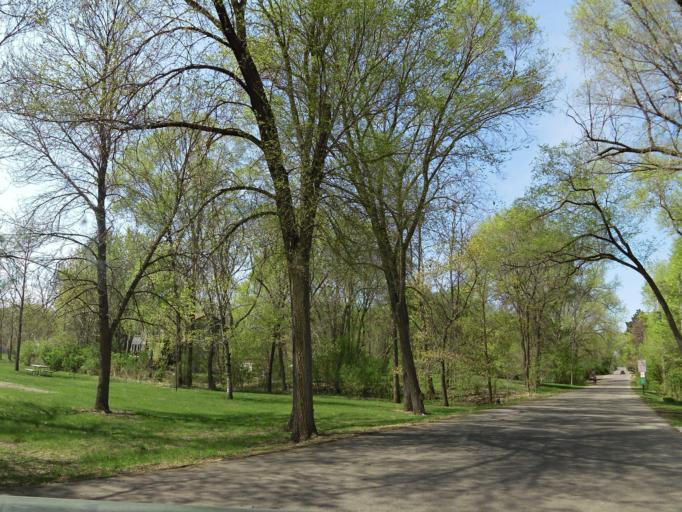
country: US
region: Minnesota
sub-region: Washington County
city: Lake Saint Croix Beach
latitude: 44.9215
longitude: -92.7642
